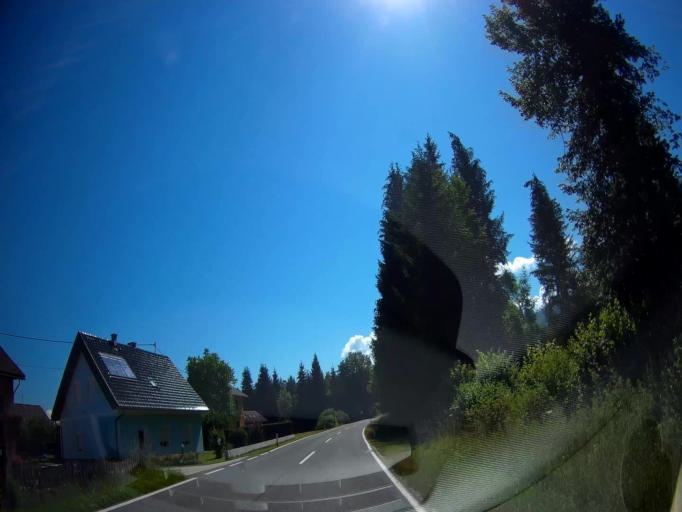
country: AT
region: Carinthia
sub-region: Politischer Bezirk Volkermarkt
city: Gallizien
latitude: 46.5444
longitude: 14.5394
